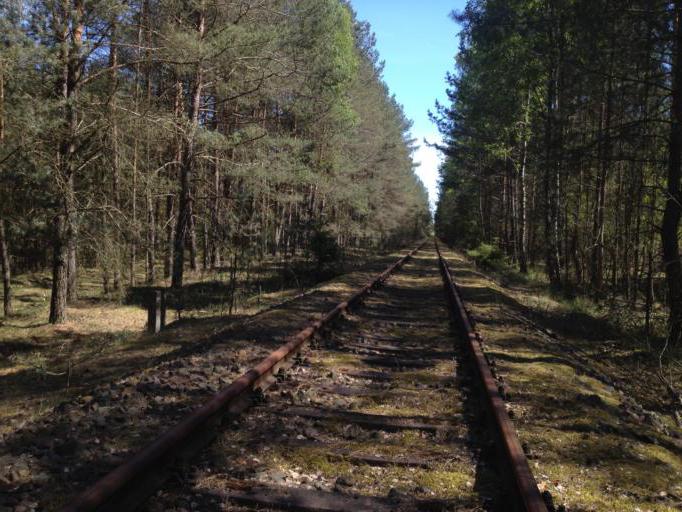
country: DE
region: Brandenburg
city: Templin
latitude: 53.1480
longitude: 13.4074
